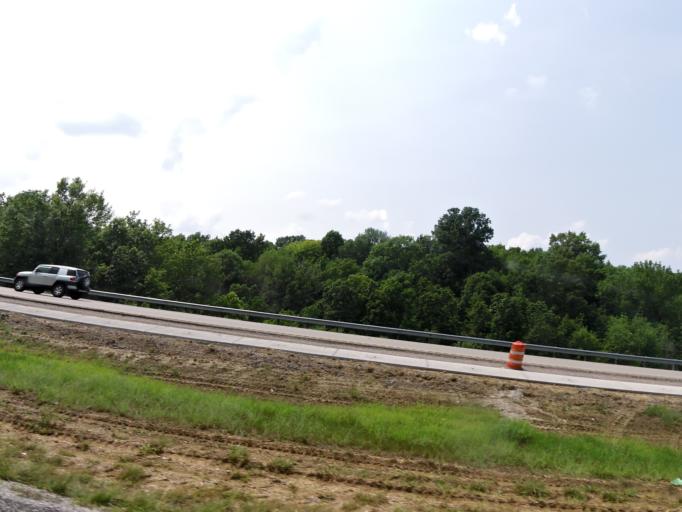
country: US
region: Kentucky
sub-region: Boone County
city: Verona
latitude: 38.8445
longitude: -84.6705
